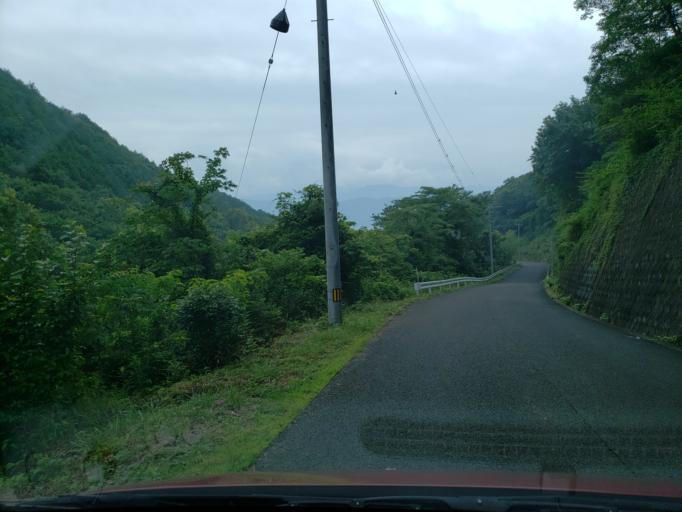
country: JP
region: Tokushima
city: Kamojimacho-jogejima
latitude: 34.1099
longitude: 134.2987
